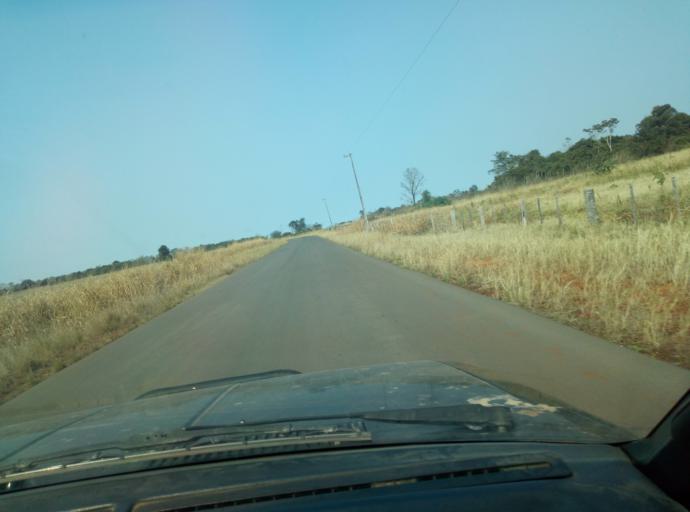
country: PY
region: Caaguazu
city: Carayao
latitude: -25.2292
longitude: -56.2891
